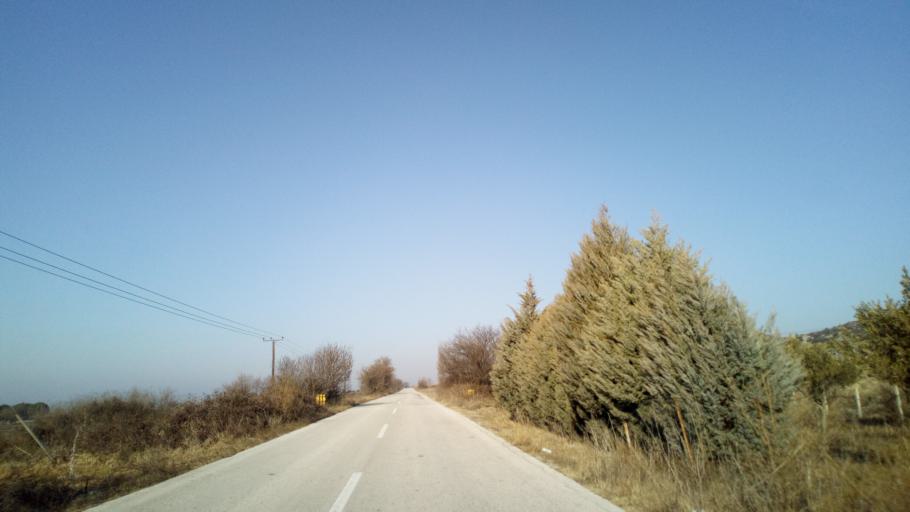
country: GR
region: Central Macedonia
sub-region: Nomos Thessalonikis
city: Gerakarou
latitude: 40.7019
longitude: 23.2001
